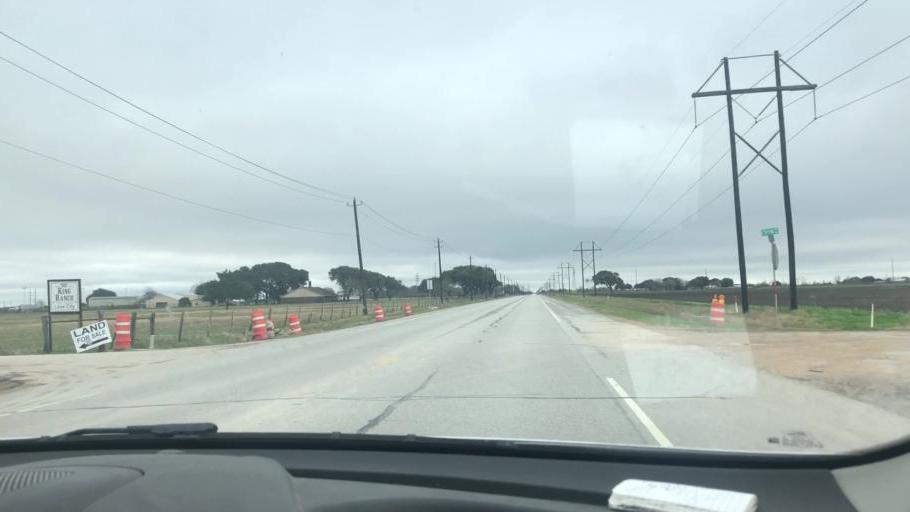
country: US
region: Texas
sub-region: Wharton County
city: Boling
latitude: 29.2053
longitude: -96.0233
